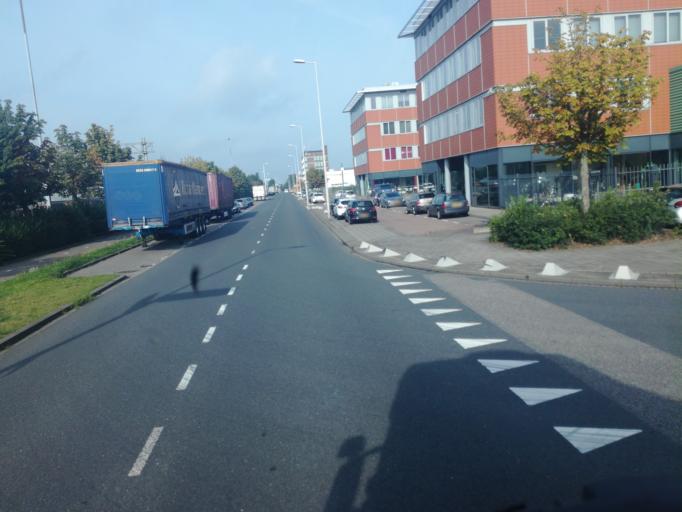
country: NL
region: South Holland
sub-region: Gemeente Albrandswaard
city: Rhoon
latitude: 51.8721
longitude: 4.4444
